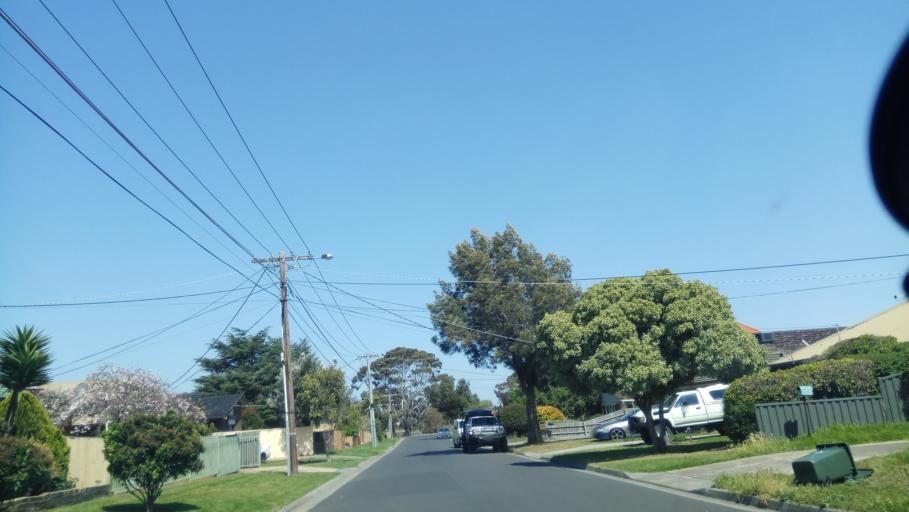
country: AU
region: Victoria
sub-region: Wyndham
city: Williams Landing
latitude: -37.8718
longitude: 144.7551
